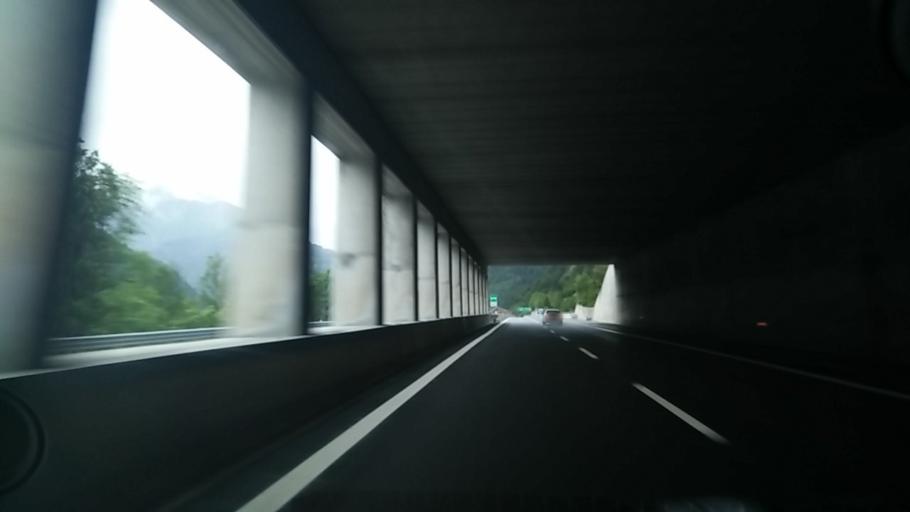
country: IT
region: Friuli Venezia Giulia
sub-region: Provincia di Udine
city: Pontebba
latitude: 46.5123
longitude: 13.3407
